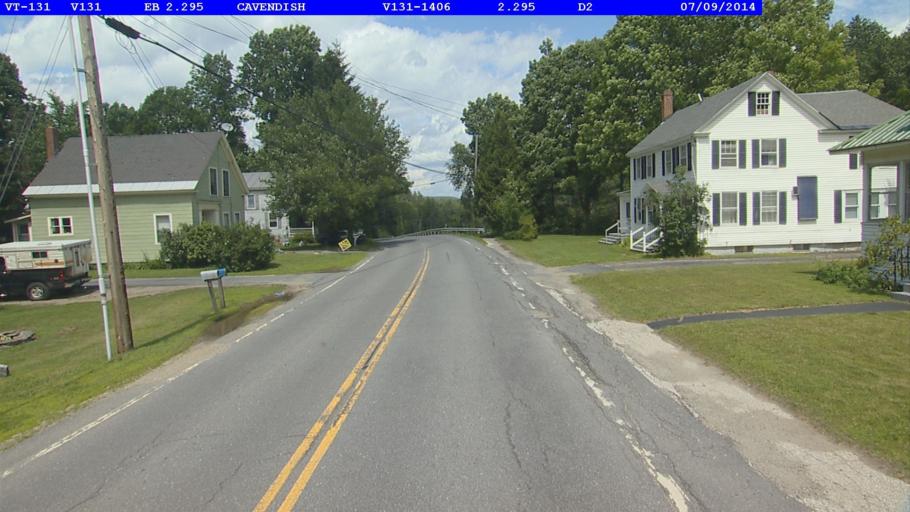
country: US
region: Vermont
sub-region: Windsor County
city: Chester
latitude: 43.3841
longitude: -72.6052
